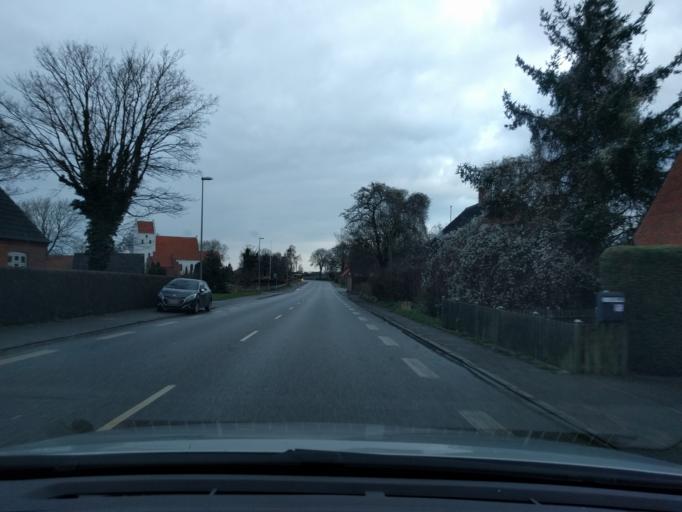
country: DK
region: Zealand
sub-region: Guldborgsund Kommune
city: Stubbekobing
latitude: 54.8036
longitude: 11.9937
